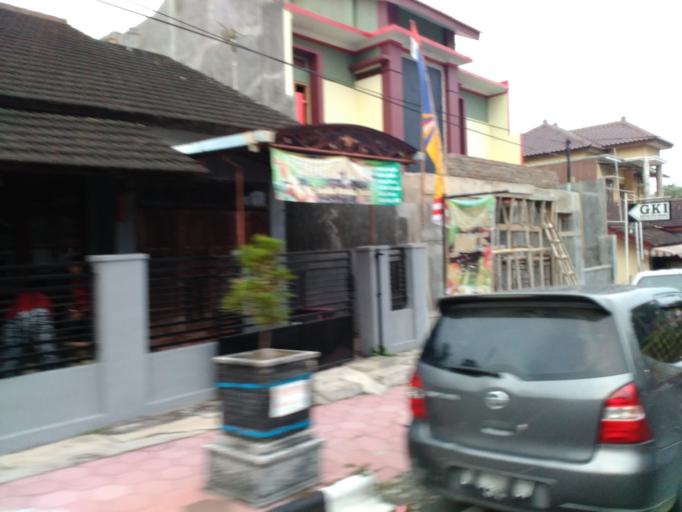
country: ID
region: Central Java
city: Boyolali
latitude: -7.5316
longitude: 110.5979
